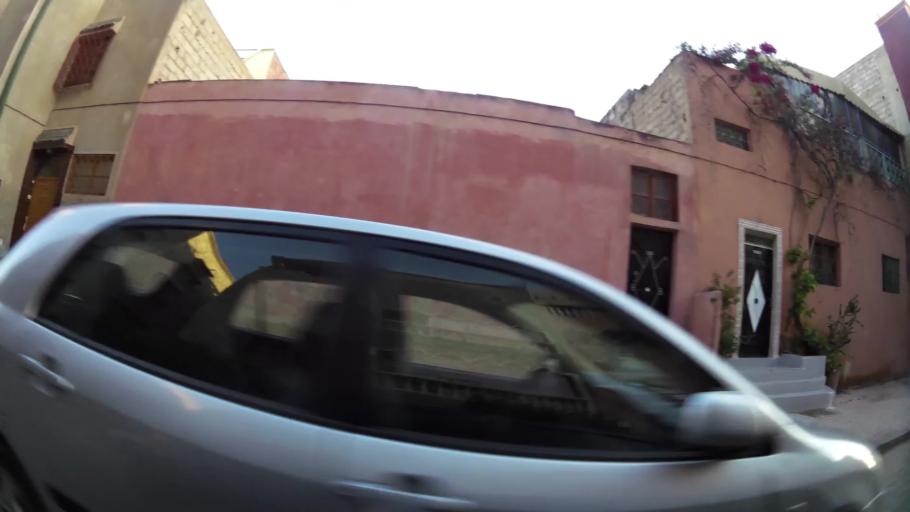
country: MA
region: Marrakech-Tensift-Al Haouz
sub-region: Marrakech
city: Marrakesh
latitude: 31.6401
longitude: -8.0368
